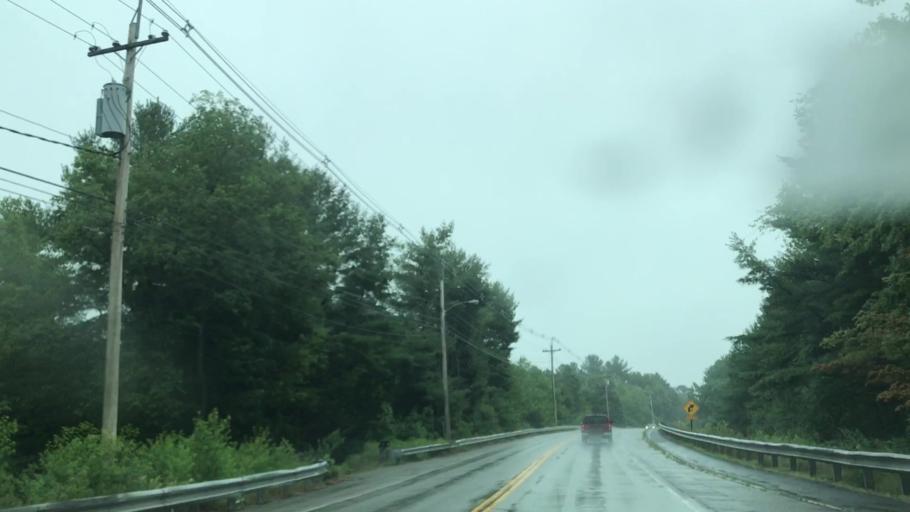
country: US
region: Maine
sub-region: York County
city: North Berwick
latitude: 43.3079
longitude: -70.7249
